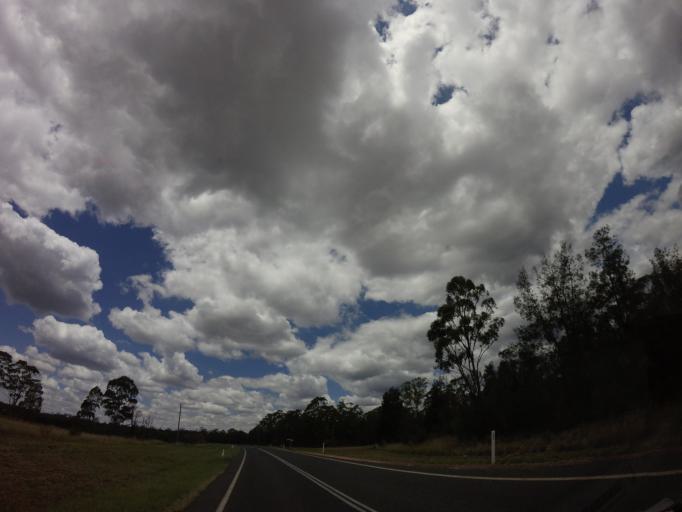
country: AU
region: Queensland
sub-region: Goondiwindi
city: Goondiwindi
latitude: -28.0074
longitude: 150.9189
